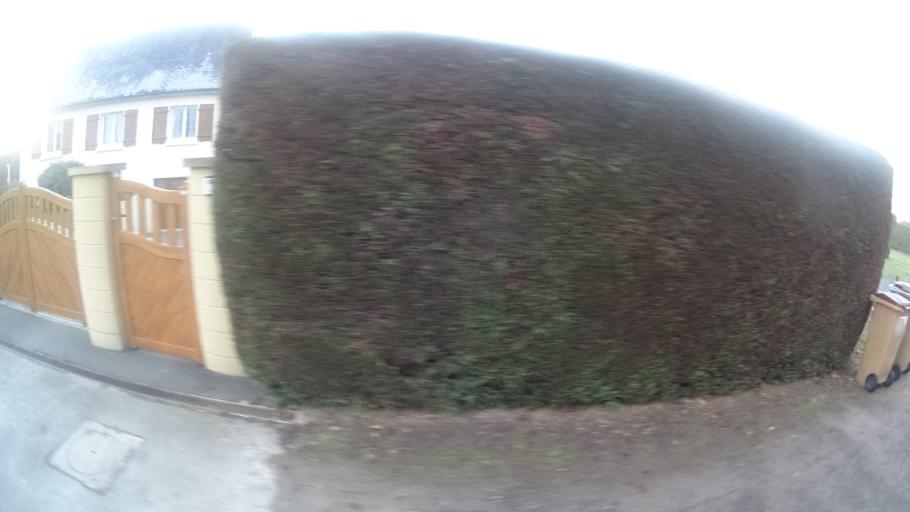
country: FR
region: Pays de la Loire
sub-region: Departement de la Loire-Atlantique
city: Saint-Nicolas-de-Redon
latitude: 47.6488
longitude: -2.0560
